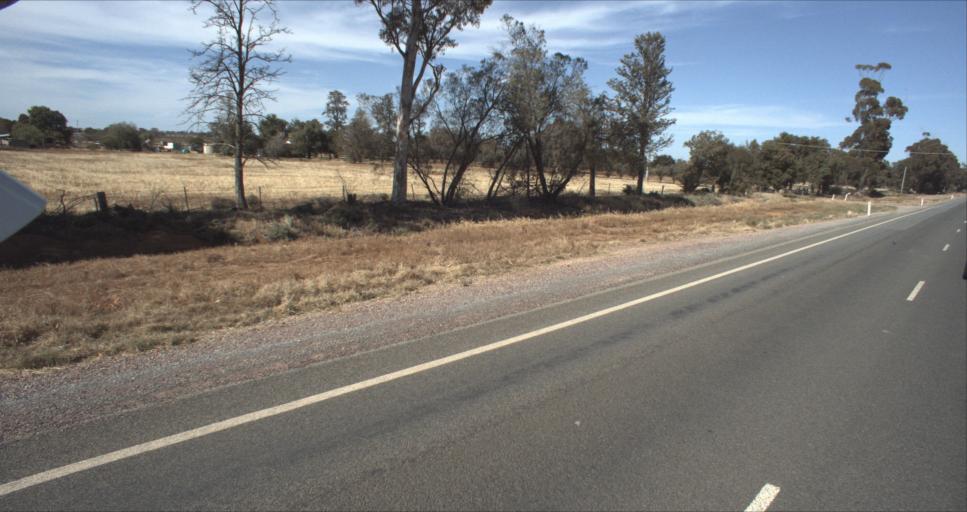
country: AU
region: New South Wales
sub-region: Leeton
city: Leeton
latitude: -34.5603
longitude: 146.4382
